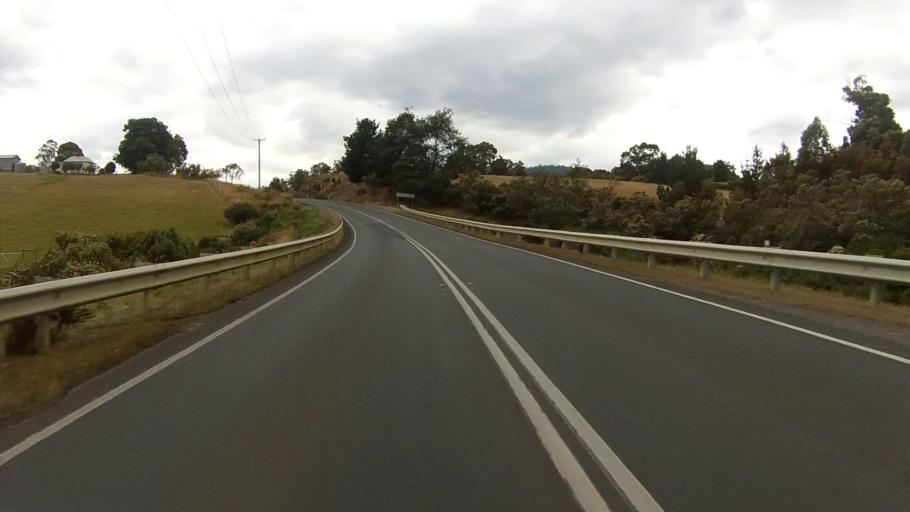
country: AU
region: Tasmania
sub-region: Huon Valley
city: Franklin
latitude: -43.1137
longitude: 147.0364
